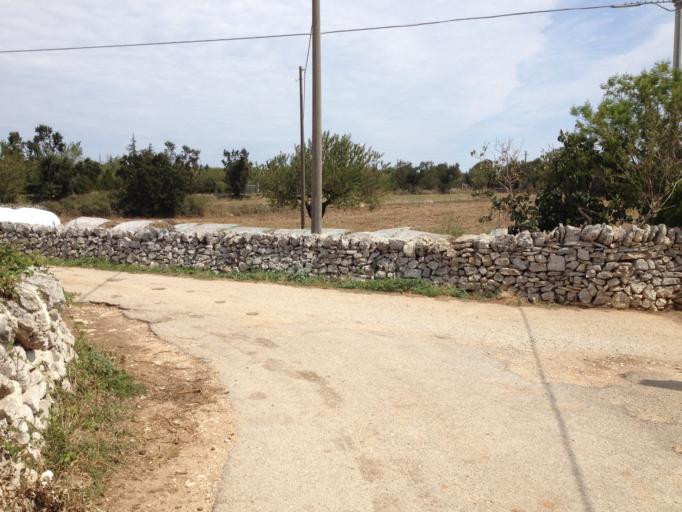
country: IT
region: Apulia
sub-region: Provincia di Bari
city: Gioia del Colle
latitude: 40.8247
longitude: 16.9799
